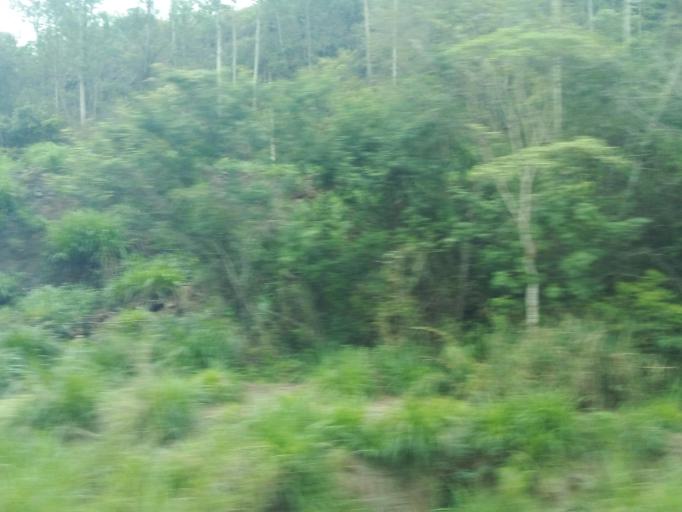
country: BR
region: Minas Gerais
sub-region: Rio Piracicaba
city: Rio Piracicaba
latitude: -19.8936
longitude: -43.1425
